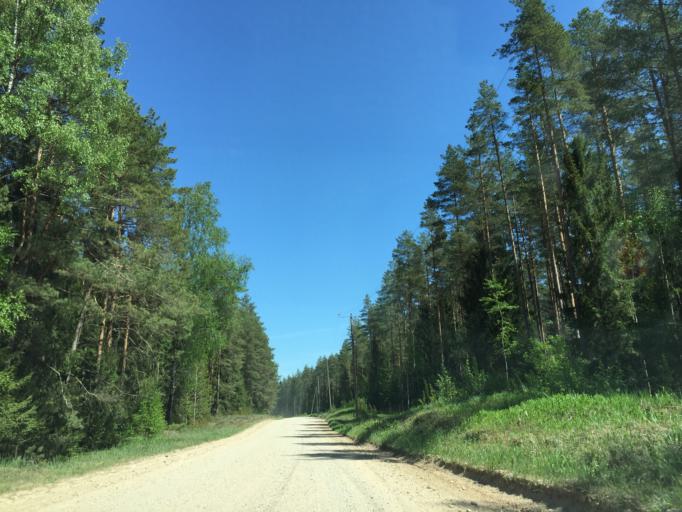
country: LV
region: Ogre
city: Ogre
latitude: 56.7456
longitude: 24.5772
